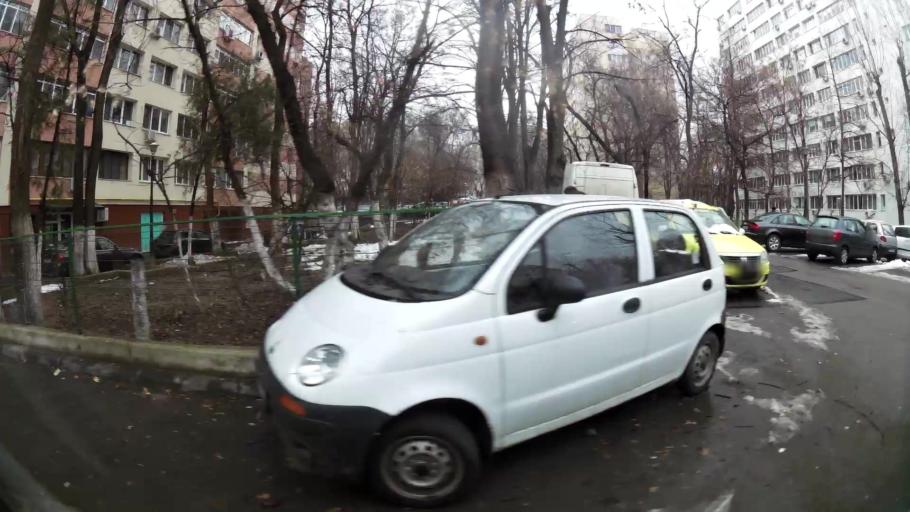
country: RO
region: Ilfov
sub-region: Comuna Popesti-Leordeni
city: Popesti-Leordeni
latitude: 44.4126
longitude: 26.1519
